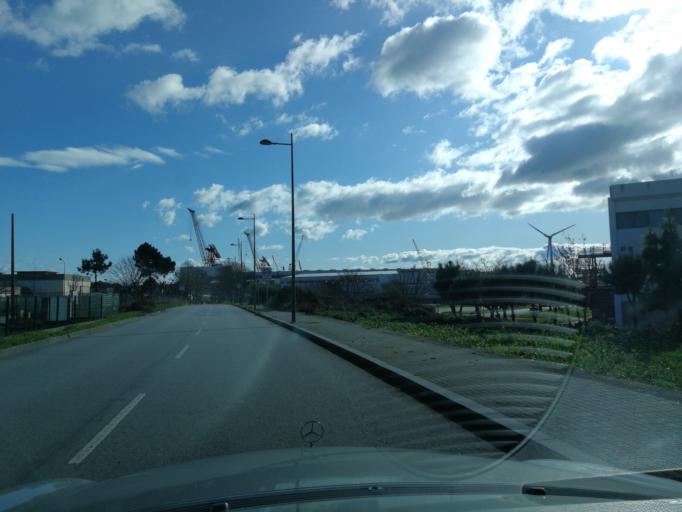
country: PT
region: Viana do Castelo
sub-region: Viana do Castelo
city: Viana do Castelo
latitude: 41.6954
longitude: -8.8463
